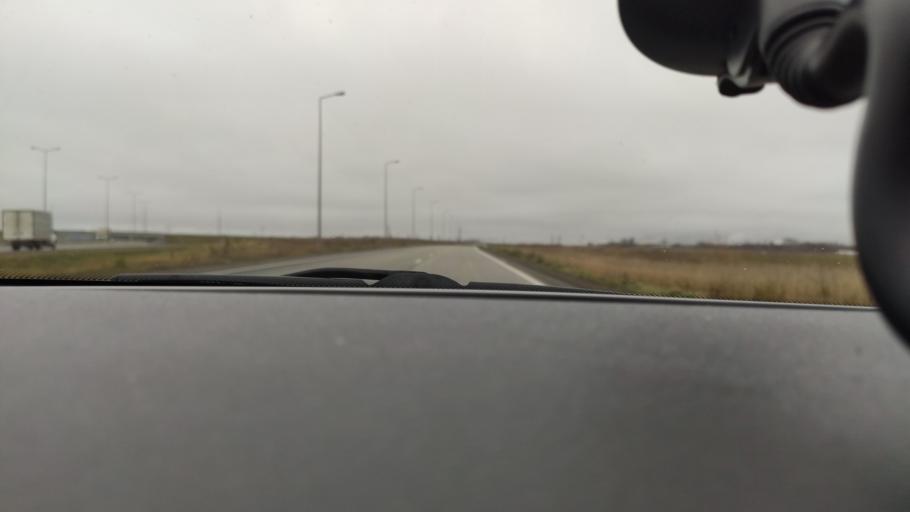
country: RU
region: Perm
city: Kondratovo
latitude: 57.9312
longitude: 56.1660
